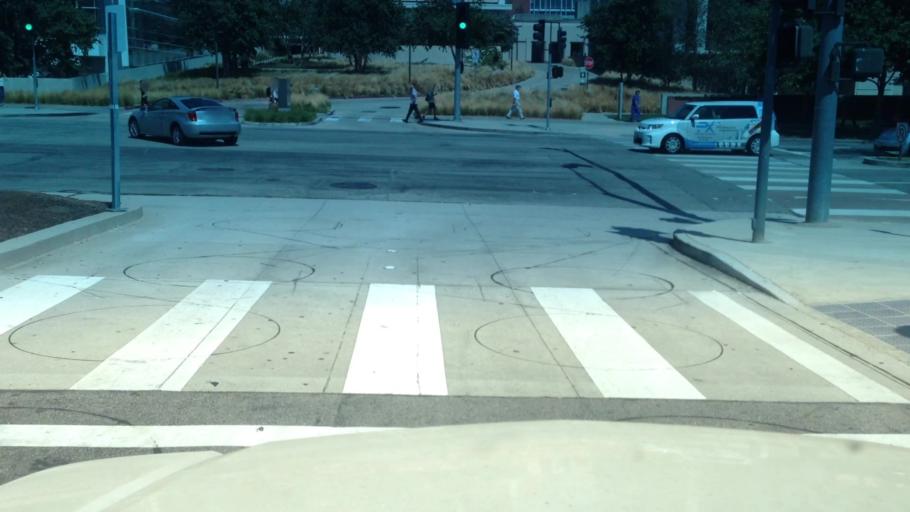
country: US
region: California
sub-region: Los Angeles County
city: Westwood, Los Angeles
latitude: 34.0649
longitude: -118.4457
